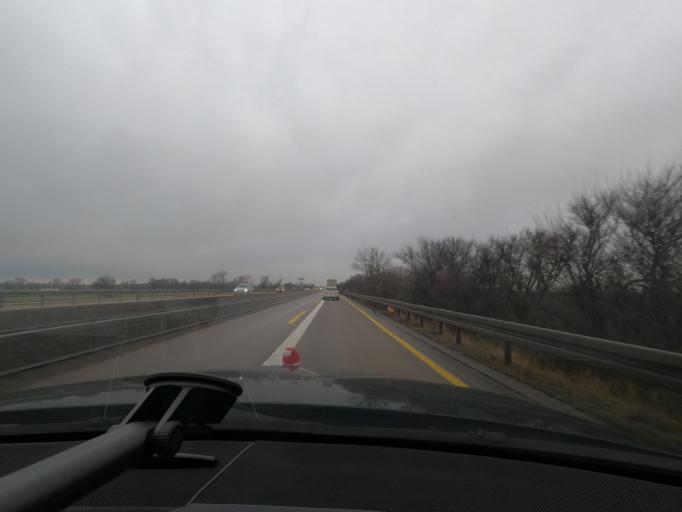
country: DE
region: Lower Saxony
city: Algermissen
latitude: 52.2423
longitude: 9.9283
